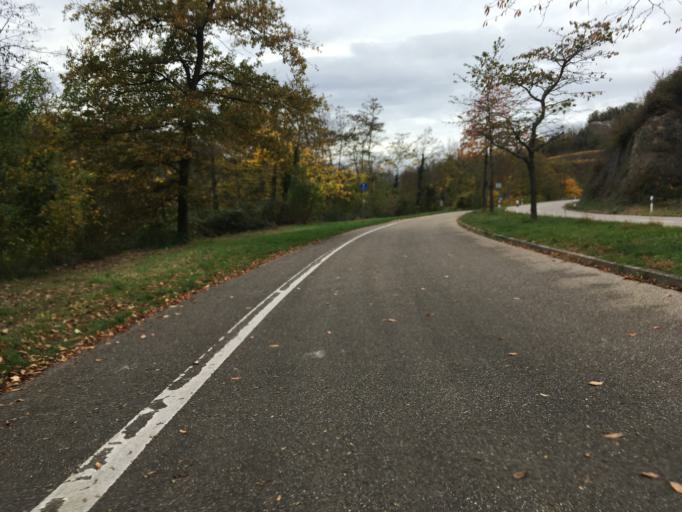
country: DE
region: Baden-Wuerttemberg
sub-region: Freiburg Region
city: Sasbach
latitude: 48.1433
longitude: 7.6104
